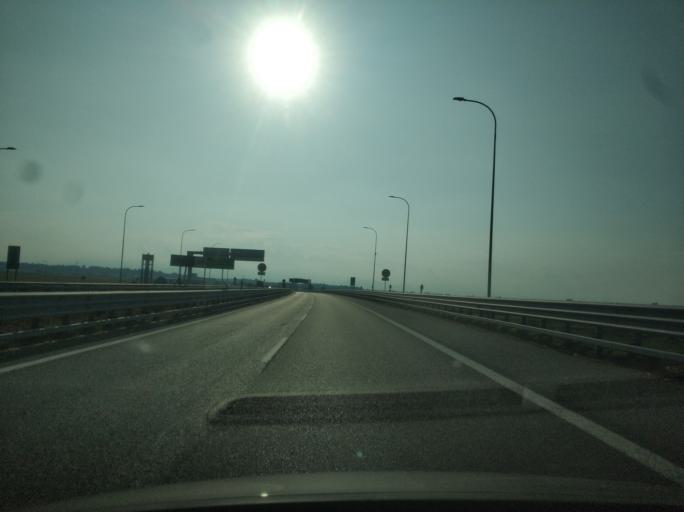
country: IT
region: Piedmont
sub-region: Provincia di Cuneo
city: Roreto
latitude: 44.6652
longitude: 7.8050
